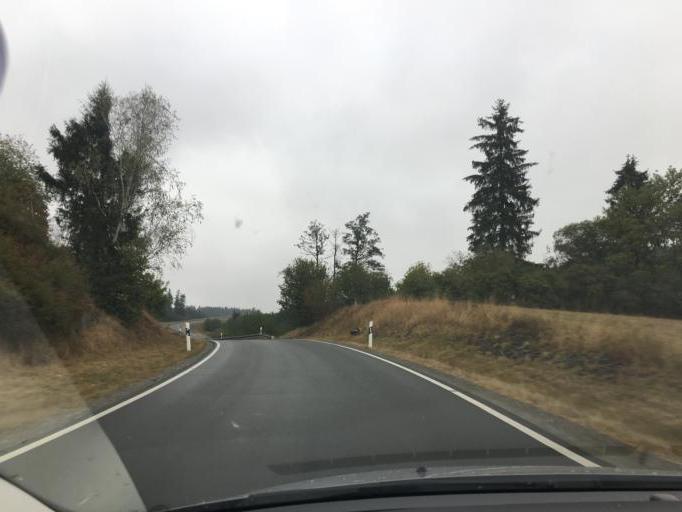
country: DE
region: Thuringia
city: Gorkwitz
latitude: 50.5646
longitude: 11.7572
